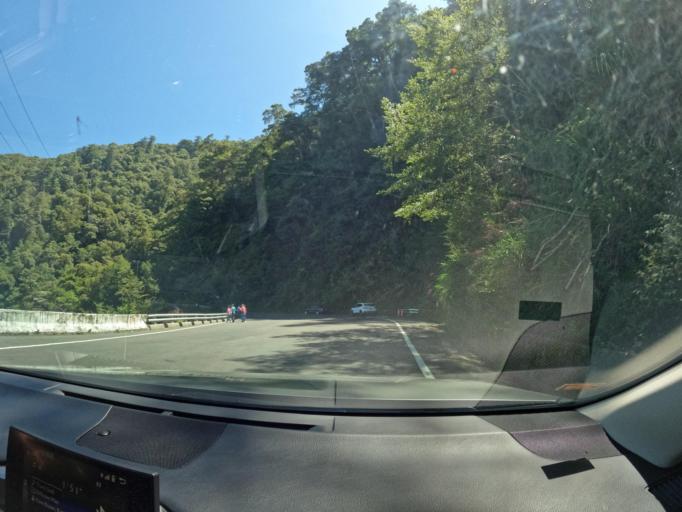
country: TW
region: Taiwan
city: Yujing
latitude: 23.2781
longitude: 120.9084
